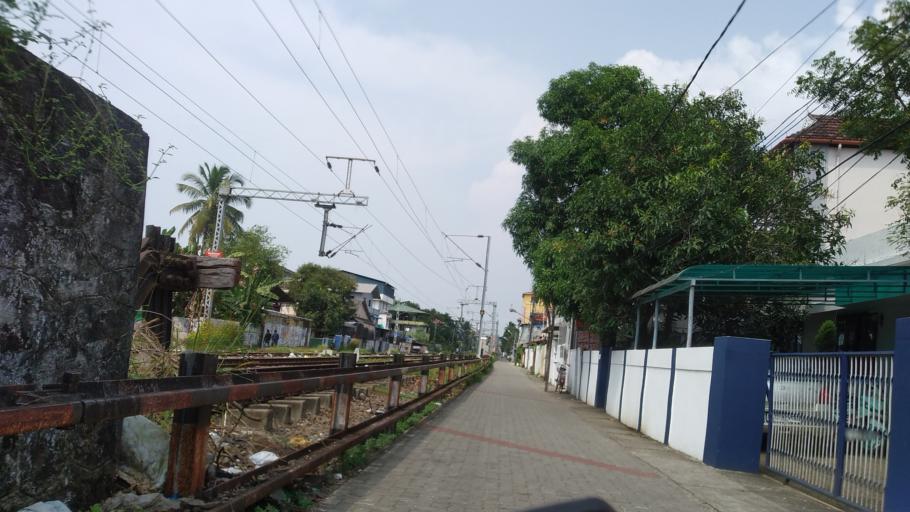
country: IN
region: Kerala
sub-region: Ernakulam
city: Cochin
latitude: 9.9592
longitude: 76.2933
